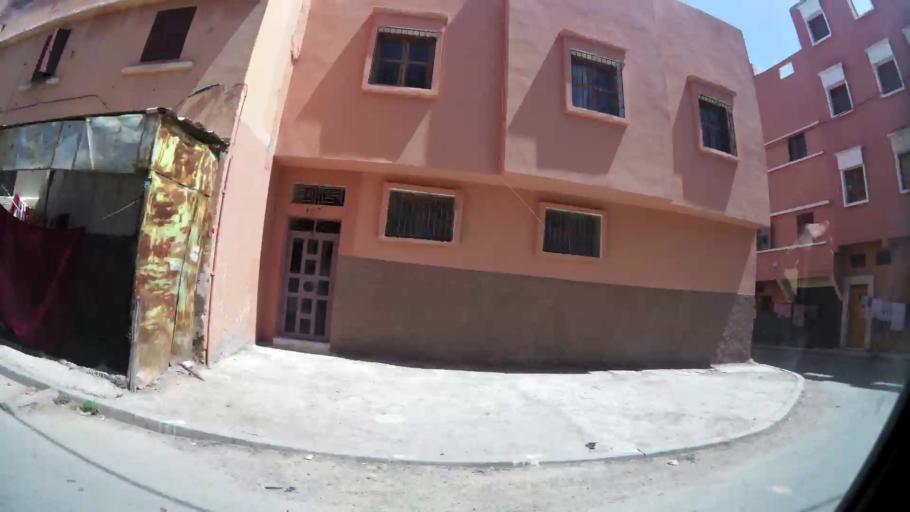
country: MA
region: Souss-Massa-Draa
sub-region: Inezgane-Ait Mellou
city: Inezgane
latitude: 30.3479
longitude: -9.4901
